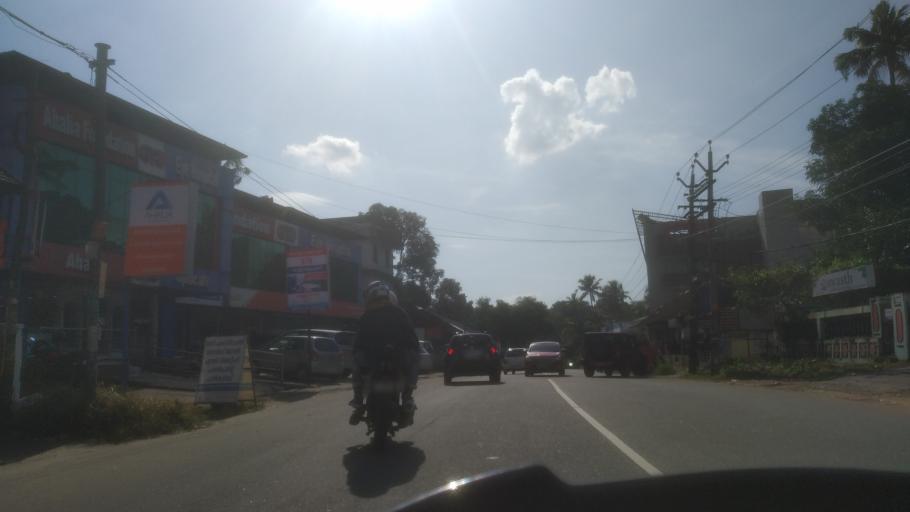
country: IN
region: Kerala
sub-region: Ernakulam
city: Muvattupula
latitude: 9.9899
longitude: 76.5729
